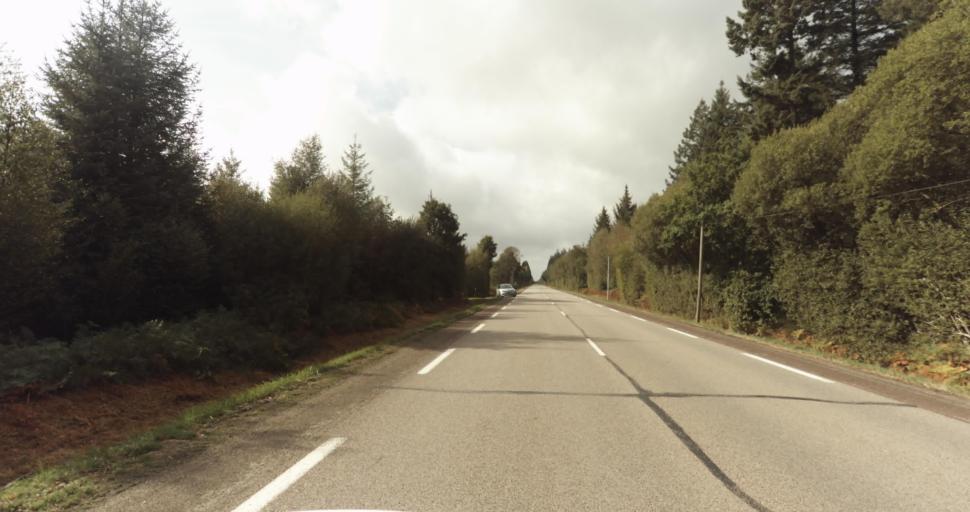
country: FR
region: Lower Normandy
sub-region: Departement de l'Orne
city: Gace
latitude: 48.8412
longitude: 0.3467
